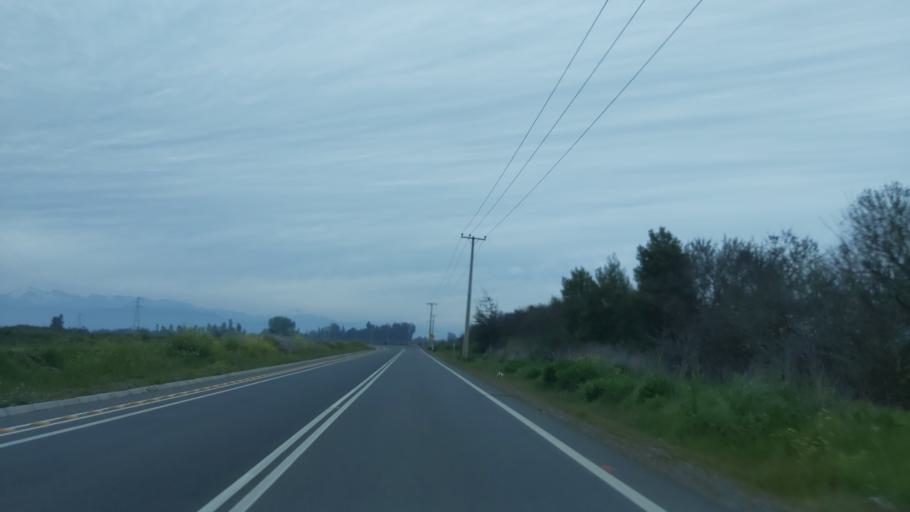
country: CL
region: Maule
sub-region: Provincia de Linares
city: Colbun
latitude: -35.7019
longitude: -71.4862
